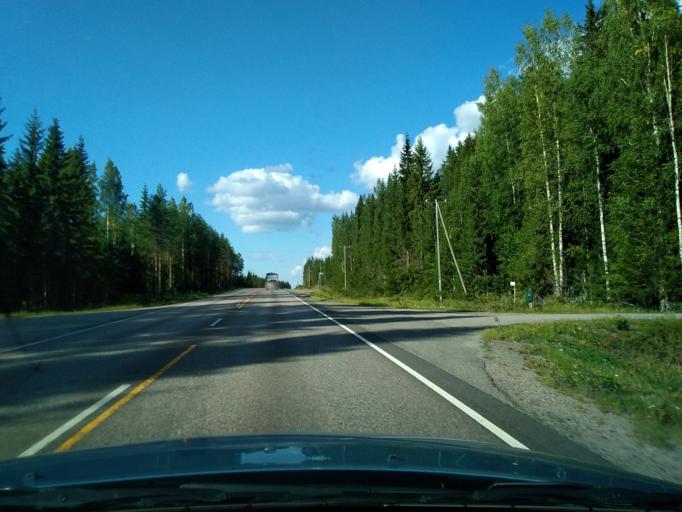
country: FI
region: Pirkanmaa
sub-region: Ylae-Pirkanmaa
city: Maenttae
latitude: 62.0762
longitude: 24.7248
